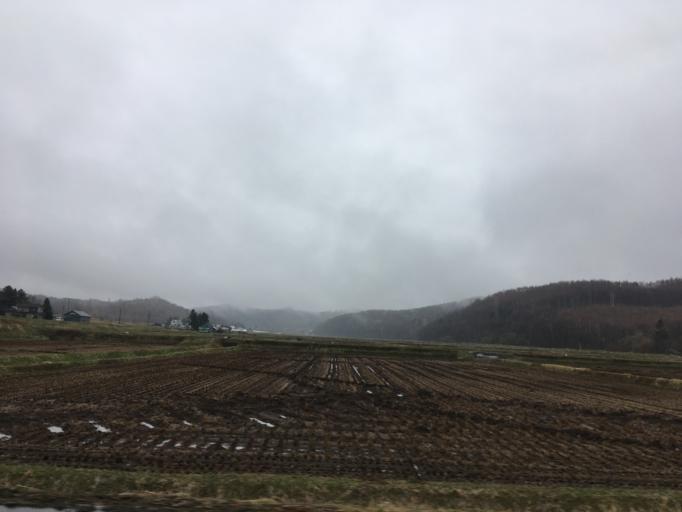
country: JP
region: Hokkaido
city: Nayoro
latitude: 44.0806
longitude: 142.4180
